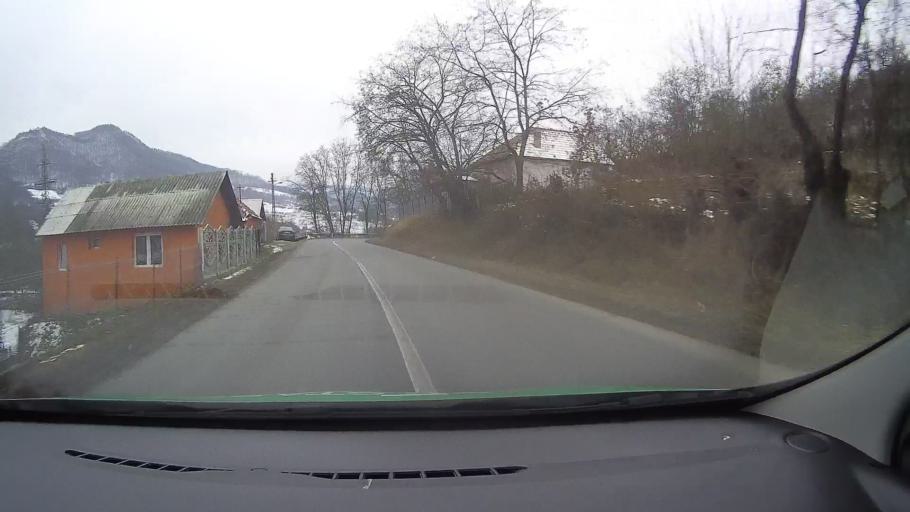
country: RO
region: Alba
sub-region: Comuna Metes
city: Metes
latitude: 46.0922
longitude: 23.4138
